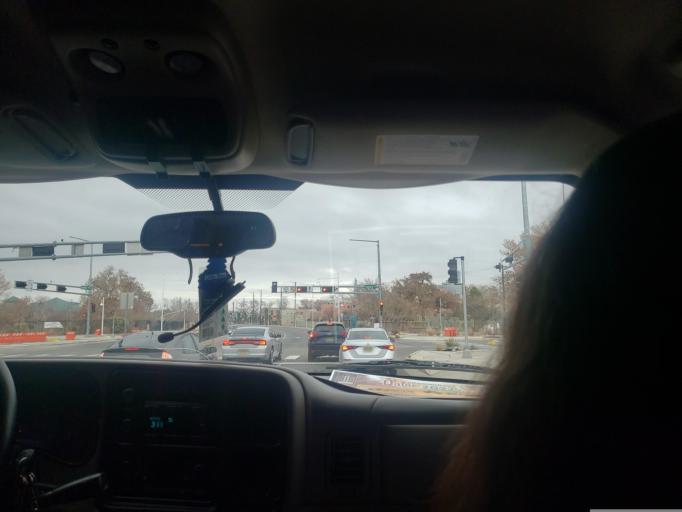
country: US
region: New Mexico
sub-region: Bernalillo County
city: Albuquerque
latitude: 35.0908
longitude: -106.6794
